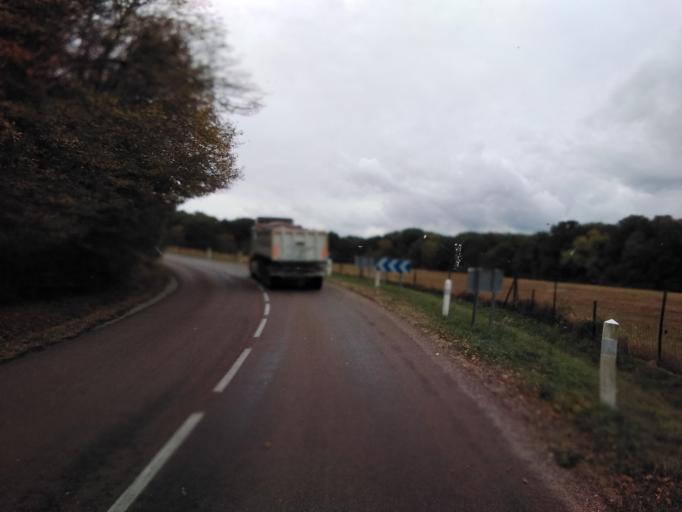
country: FR
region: Champagne-Ardenne
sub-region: Departement de l'Aube
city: Vendeuvre-sur-Barse
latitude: 48.2607
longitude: 4.4926
